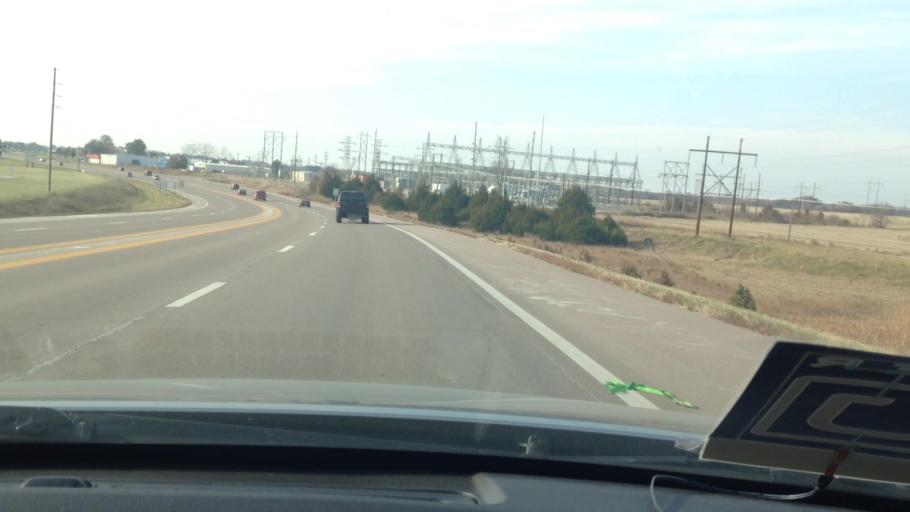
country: US
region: Missouri
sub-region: Henry County
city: Clinton
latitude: 38.3864
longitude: -93.7570
